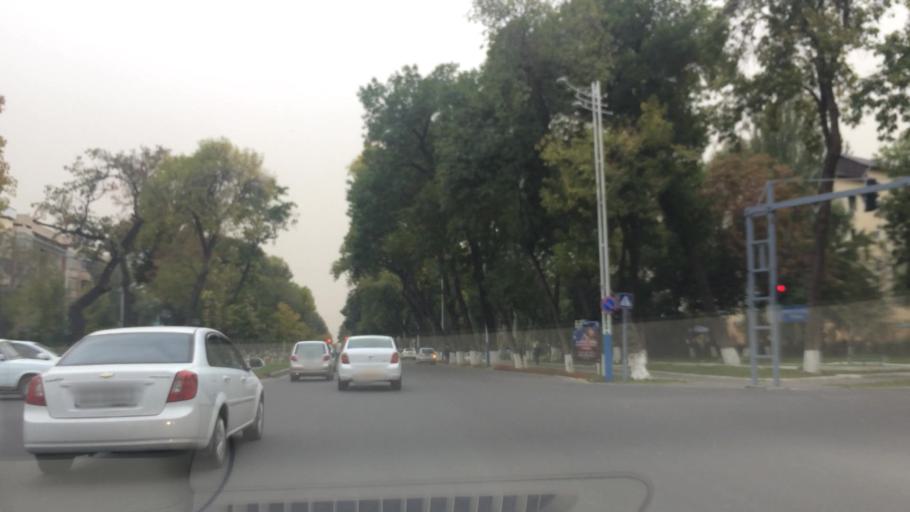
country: UZ
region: Toshkent Shahri
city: Tashkent
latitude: 41.3077
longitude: 69.2924
